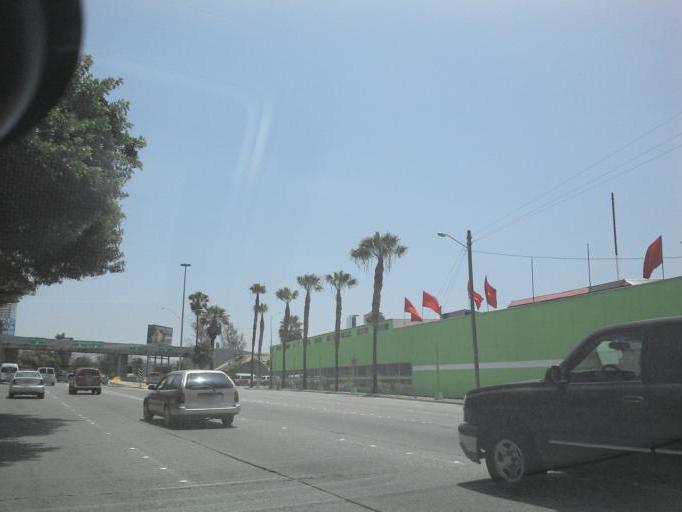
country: MX
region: Baja California
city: Tijuana
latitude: 32.5359
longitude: -117.0319
